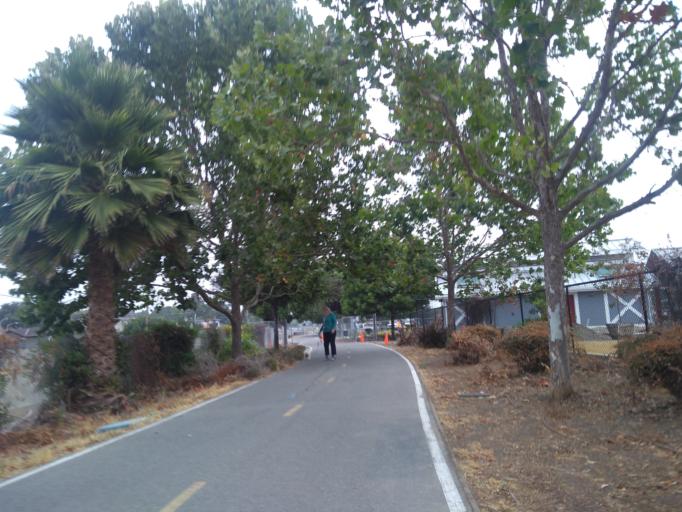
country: US
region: California
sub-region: Santa Clara County
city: Santa Clara
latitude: 37.3627
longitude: -121.9685
